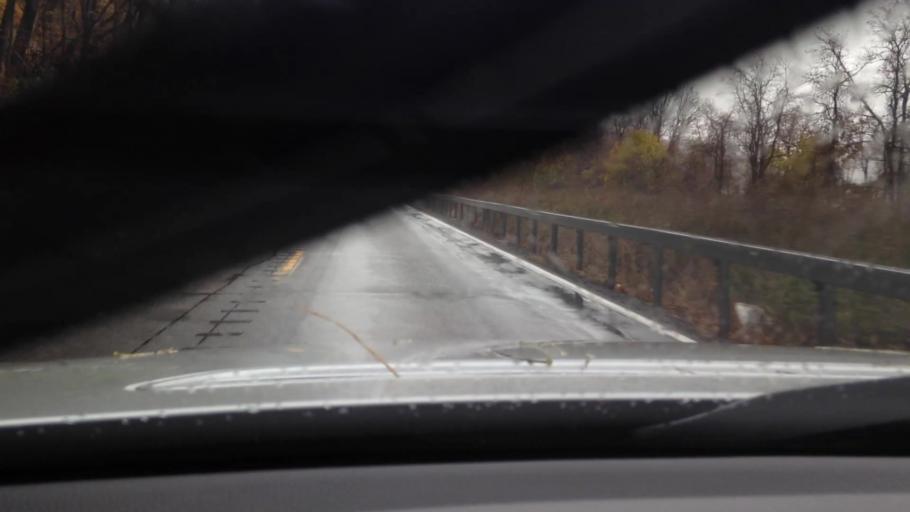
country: US
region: New York
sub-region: Putnam County
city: Cold Spring
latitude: 41.4323
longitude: -73.9697
